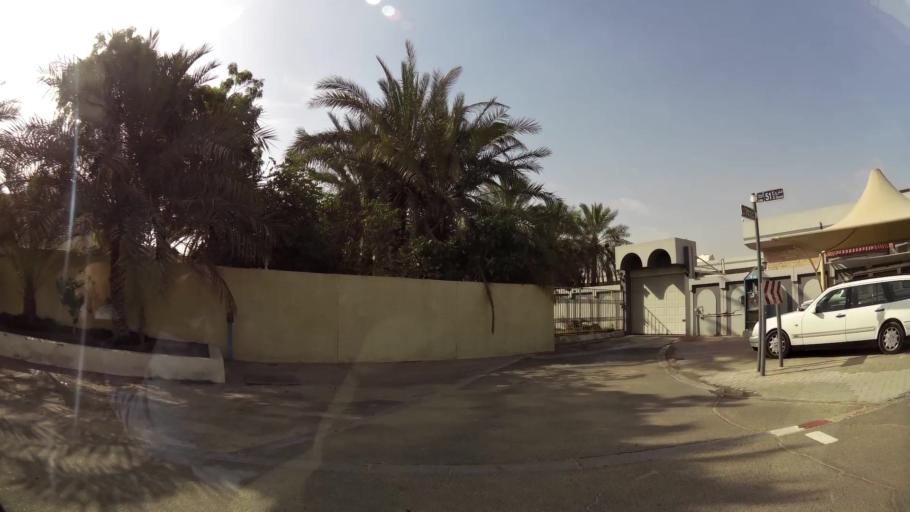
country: AE
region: Ash Shariqah
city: Sharjah
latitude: 25.2247
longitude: 55.4030
